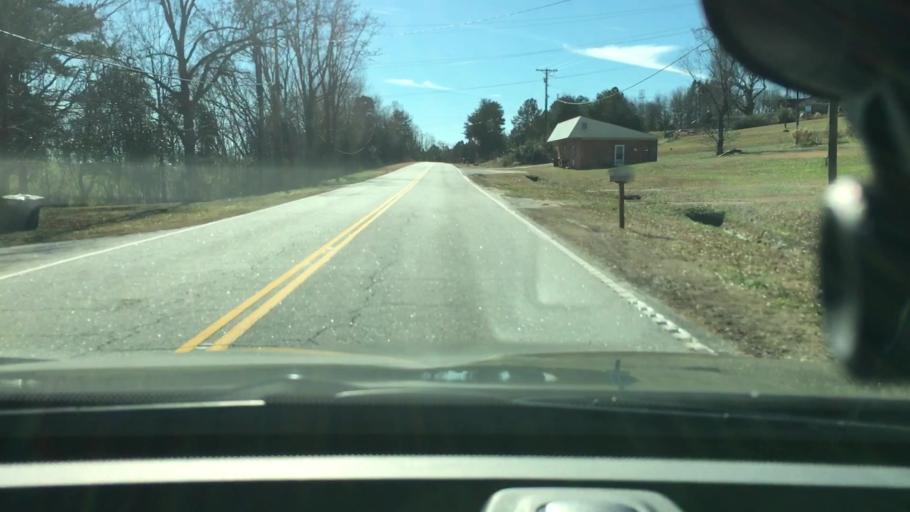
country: US
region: South Carolina
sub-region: Cherokee County
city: Gaffney
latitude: 35.0370
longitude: -81.6783
